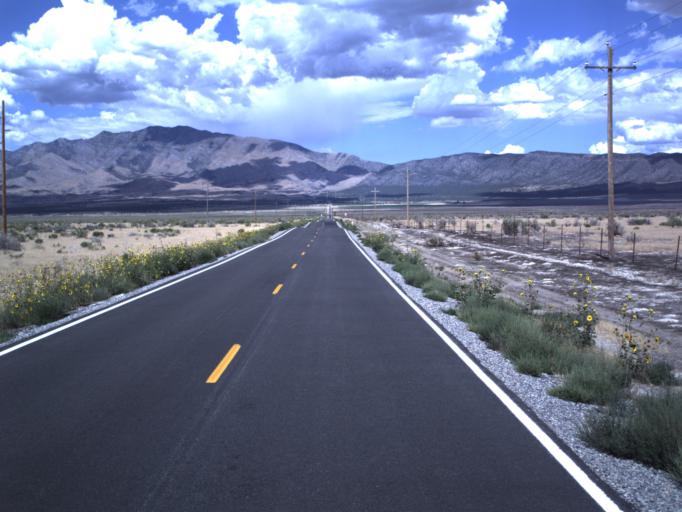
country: US
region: Utah
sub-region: Tooele County
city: Grantsville
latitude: 40.2564
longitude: -112.6968
